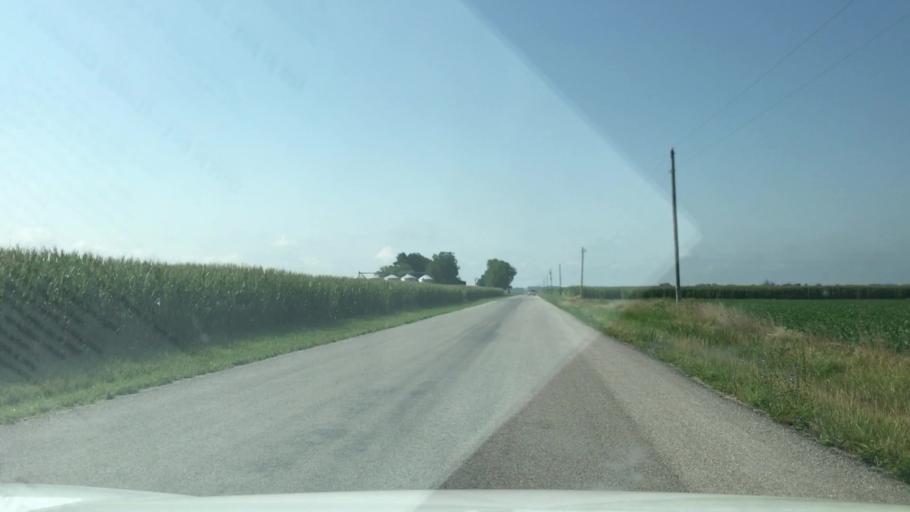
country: US
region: Illinois
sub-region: Washington County
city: Okawville
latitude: 38.4212
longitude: -89.4777
